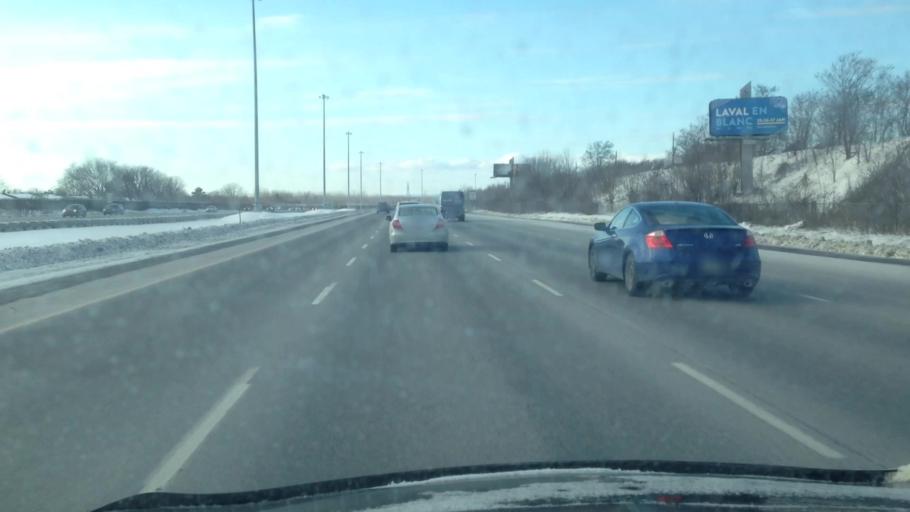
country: CA
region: Quebec
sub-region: Laurentides
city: Rosemere
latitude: 45.5885
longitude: -73.7931
